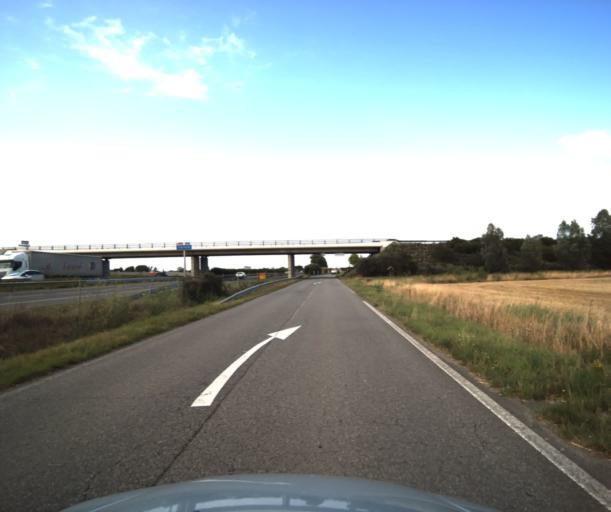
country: FR
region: Midi-Pyrenees
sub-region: Departement de la Haute-Garonne
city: Le Fauga
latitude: 43.4307
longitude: 1.3077
